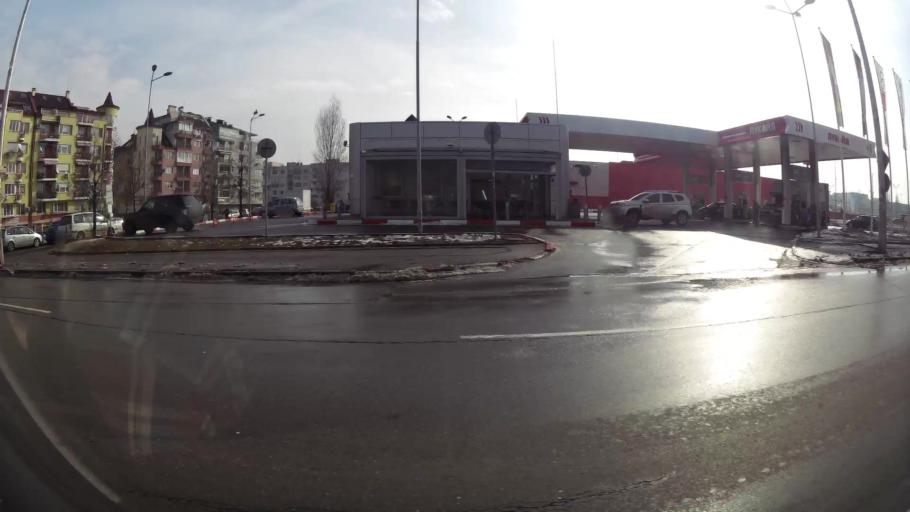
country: BG
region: Sofiya
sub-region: Obshtina Bozhurishte
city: Bozhurishte
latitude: 42.7207
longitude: 23.2558
